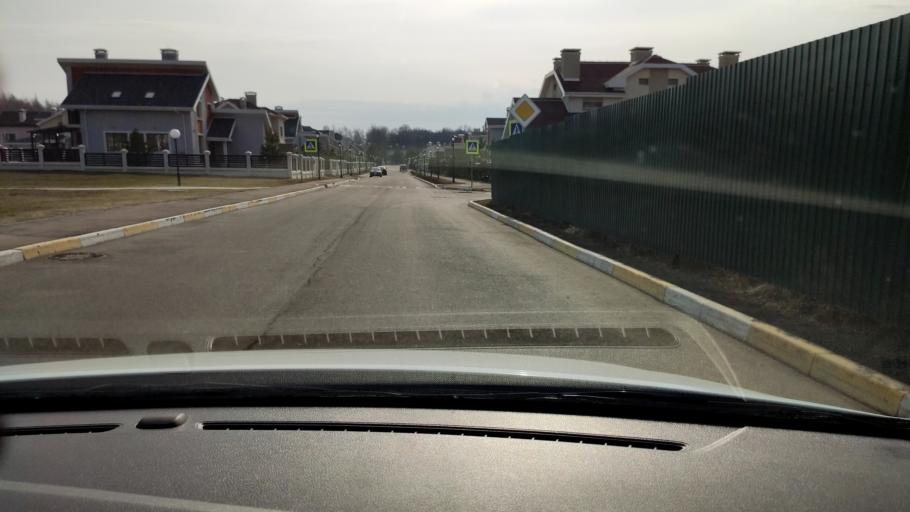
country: RU
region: Tatarstan
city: Stolbishchi
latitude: 55.7130
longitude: 49.2150
